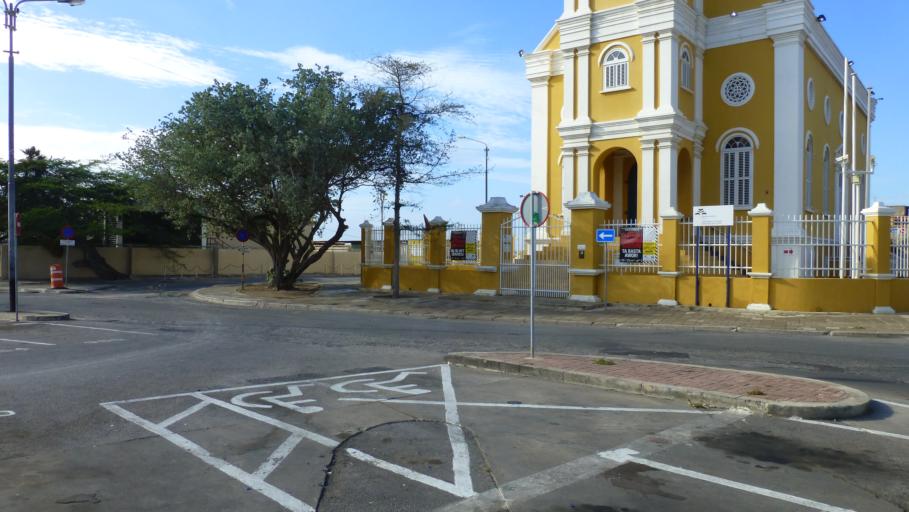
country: CW
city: Willemstad
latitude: 12.1040
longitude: -68.9329
